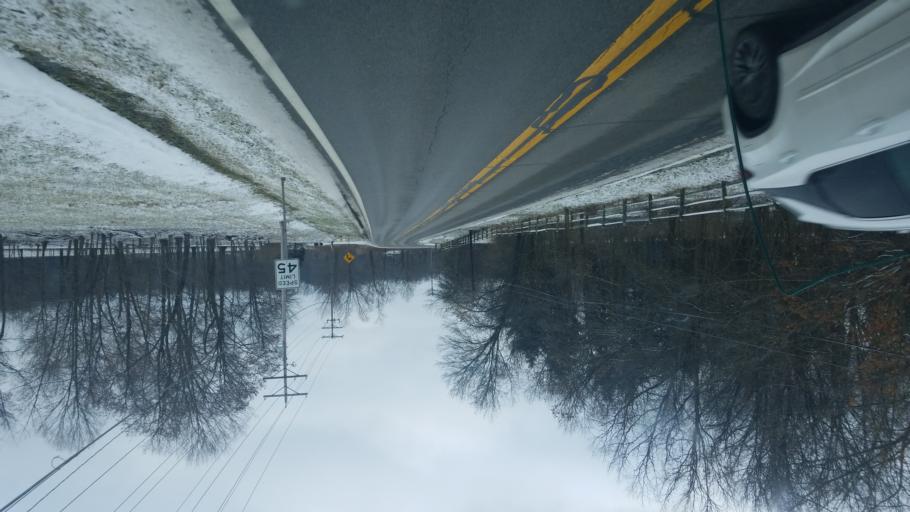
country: US
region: Ohio
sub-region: Franklin County
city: Gahanna
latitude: 40.0332
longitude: -82.8415
